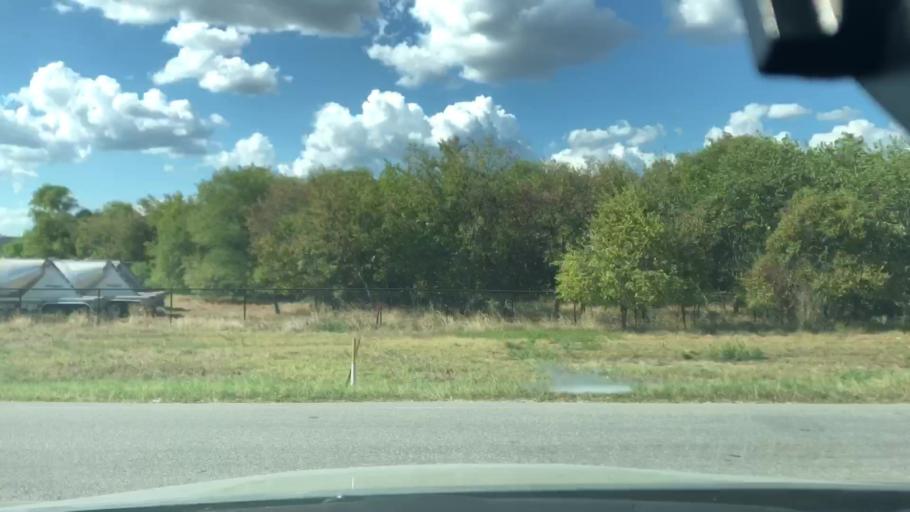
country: US
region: Texas
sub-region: Comal County
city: New Braunfels
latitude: 29.6648
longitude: -98.1732
